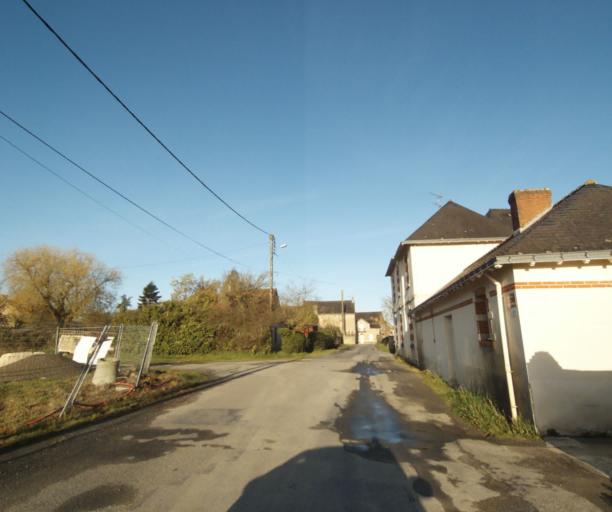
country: FR
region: Pays de la Loire
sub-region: Departement de la Loire-Atlantique
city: Bouvron
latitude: 47.4157
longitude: -1.8452
